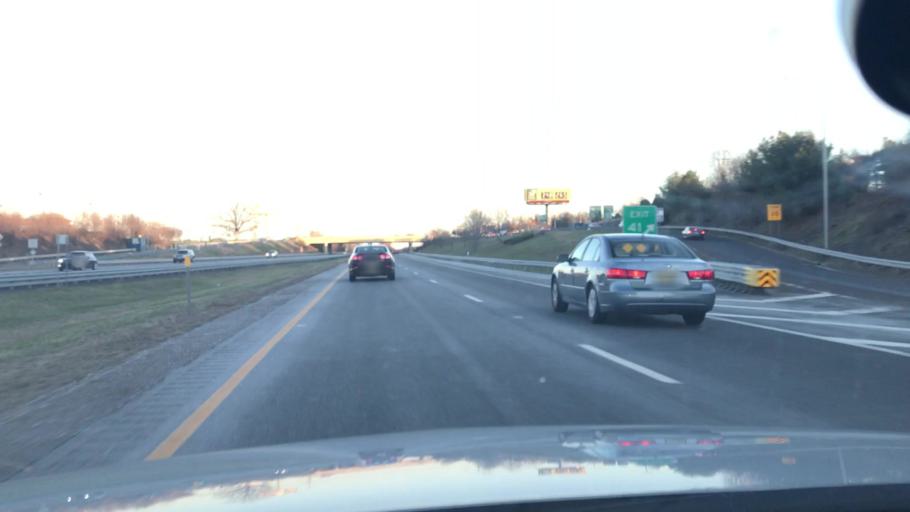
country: US
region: New Jersey
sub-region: Camden County
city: Sicklerville
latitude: 39.7354
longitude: -75.0109
